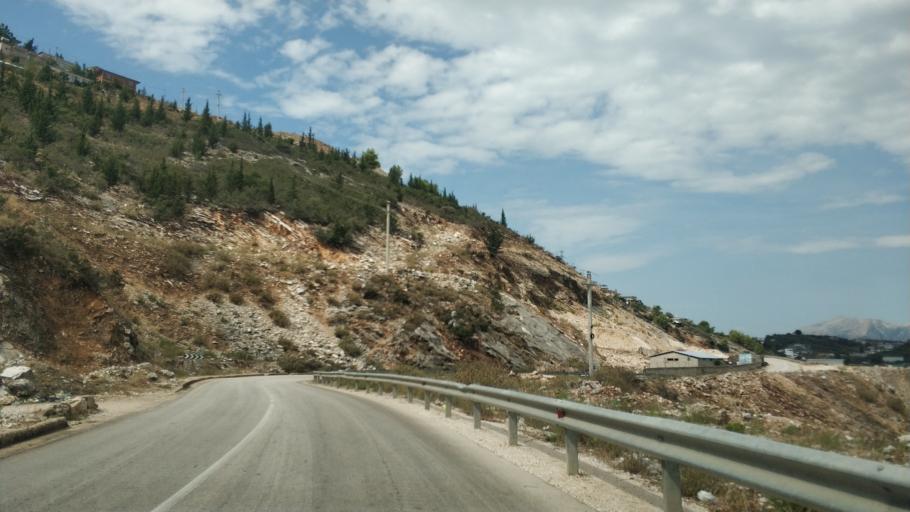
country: AL
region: Vlore
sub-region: Rrethi i Sarandes
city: Sarande
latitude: 39.8637
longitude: 20.0336
